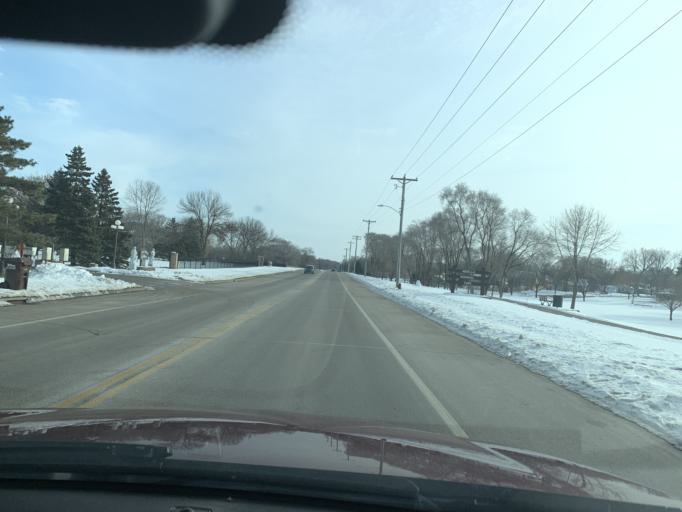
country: US
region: Minnesota
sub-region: Washington County
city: Saint Paul Park
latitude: 44.8428
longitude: -92.9823
